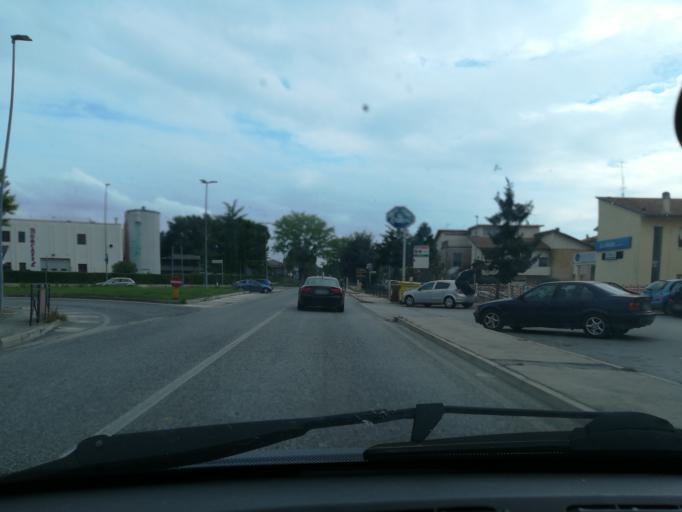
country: IT
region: The Marches
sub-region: Provincia di Macerata
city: Piediripa
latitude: 43.2749
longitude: 13.4929
